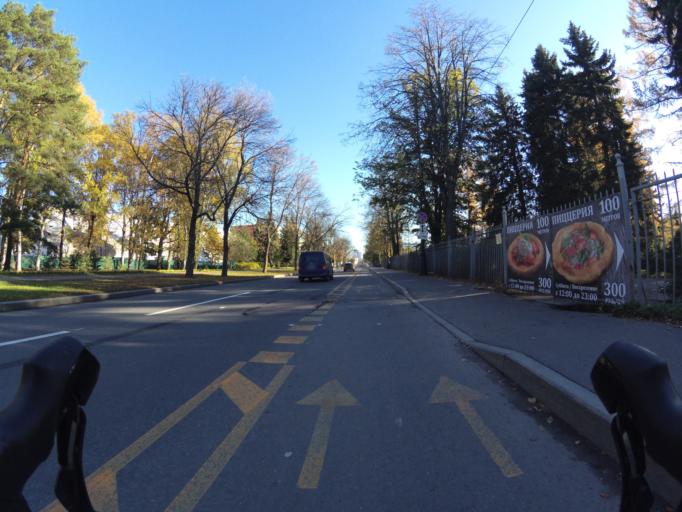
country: RU
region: Leningrad
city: Krestovskiy ostrov
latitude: 59.9738
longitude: 30.2512
